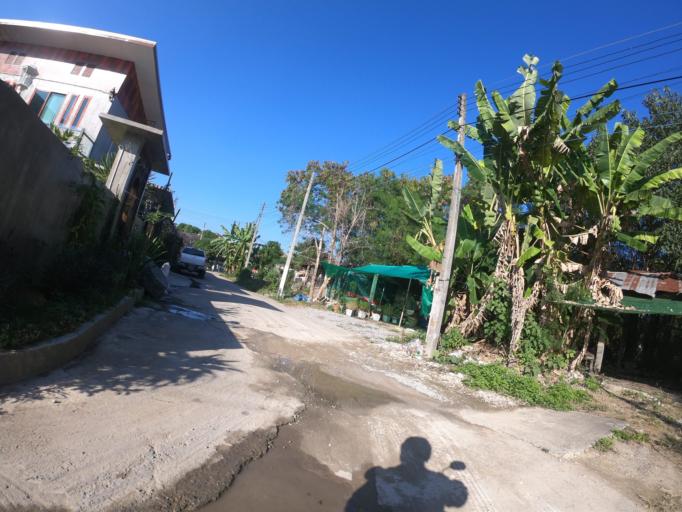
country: TH
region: Chiang Mai
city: Chiang Mai
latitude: 18.7527
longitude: 98.9788
